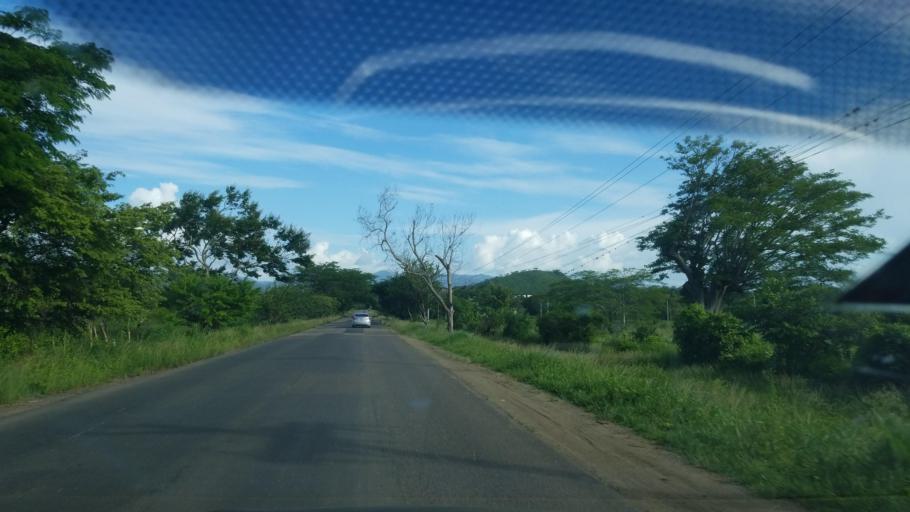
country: HN
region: El Paraiso
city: Arauli
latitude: 13.9528
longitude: -86.5610
